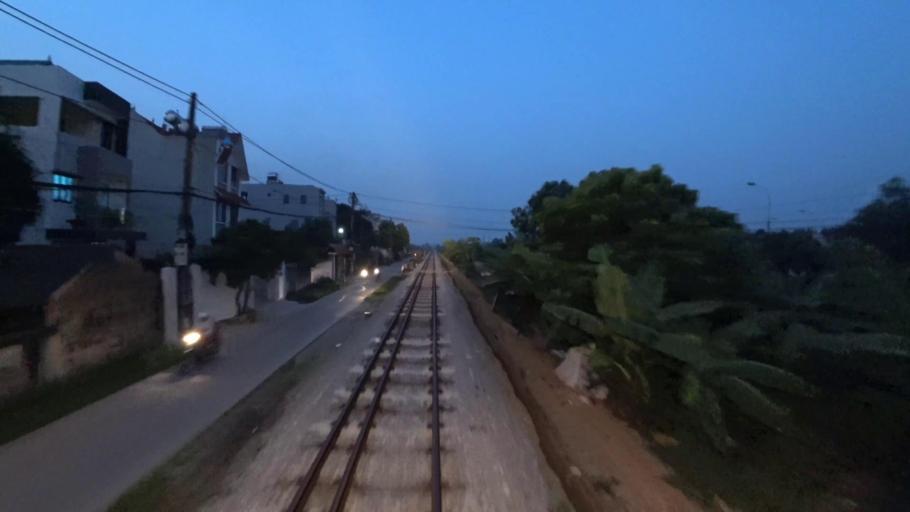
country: VN
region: Ha Noi
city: Soc Son
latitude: 21.2593
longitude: 105.8620
